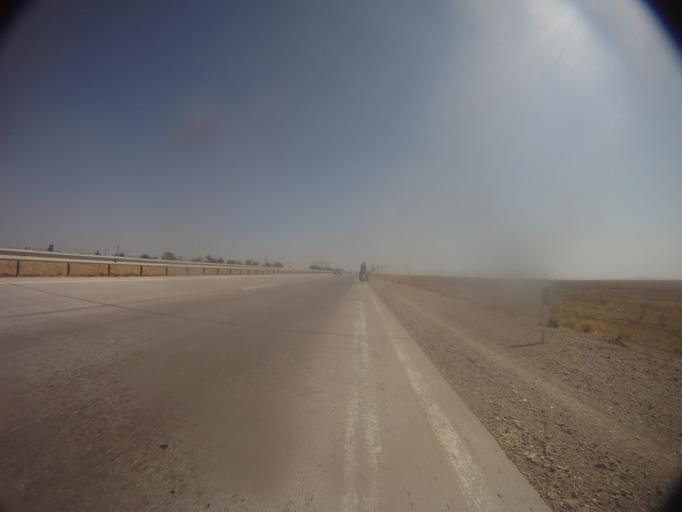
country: KZ
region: Zhambyl
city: Taraz
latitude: 42.7957
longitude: 71.0828
